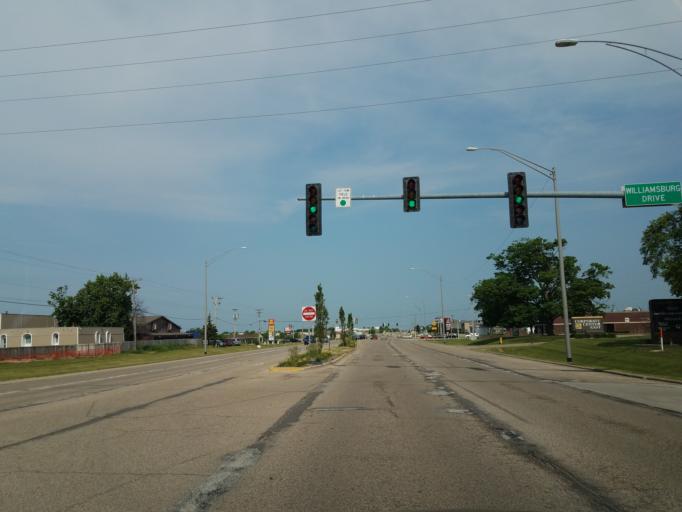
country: US
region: Illinois
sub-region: McLean County
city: Bloomington
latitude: 40.4883
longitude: -88.9454
